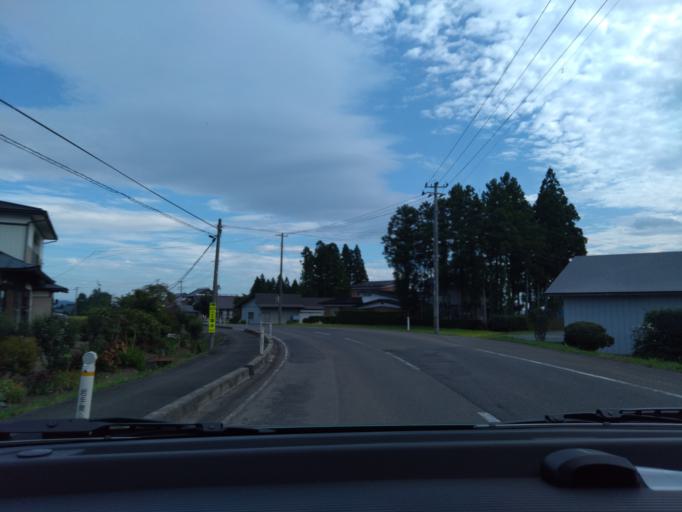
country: JP
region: Iwate
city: Kitakami
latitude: 39.3302
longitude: 141.0557
